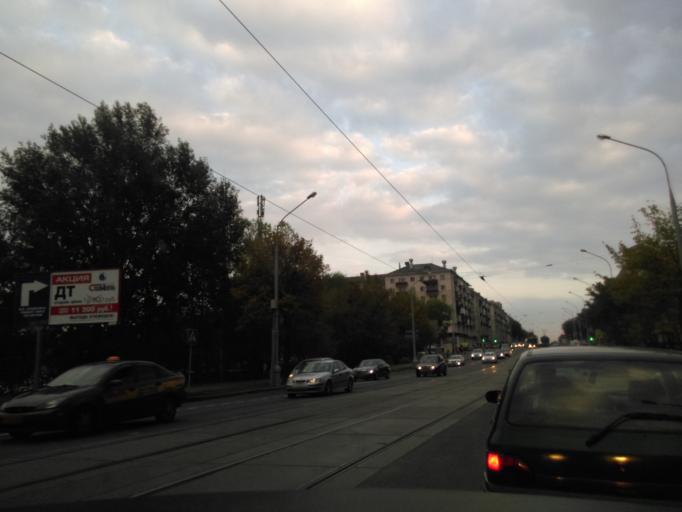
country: BY
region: Minsk
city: Minsk
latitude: 53.9027
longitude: 27.6003
